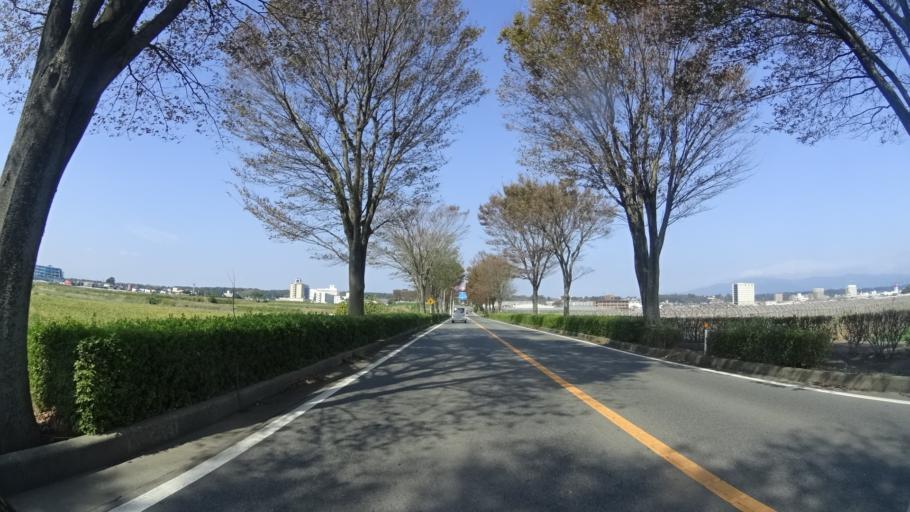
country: JP
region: Kumamoto
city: Ozu
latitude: 32.8703
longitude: 130.8553
